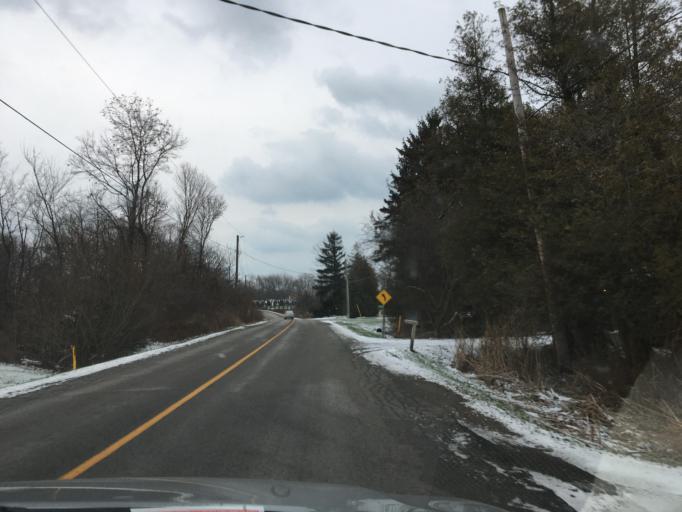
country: CA
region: Ontario
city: Norfolk County
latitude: 42.7877
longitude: -80.1610
